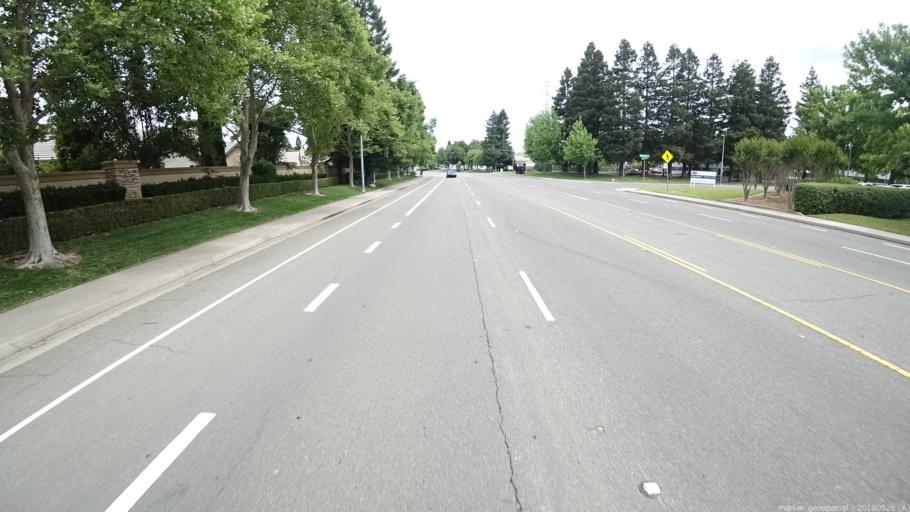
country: US
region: California
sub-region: Yolo County
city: West Sacramento
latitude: 38.6118
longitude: -121.5174
